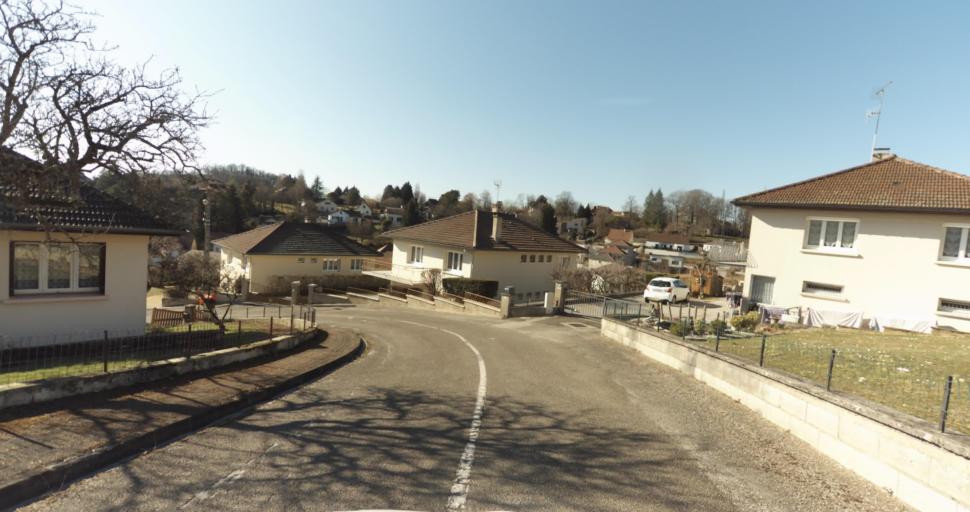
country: FR
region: Franche-Comte
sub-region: Departement du Jura
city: Lons-le-Saunier
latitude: 46.6813
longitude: 5.5409
